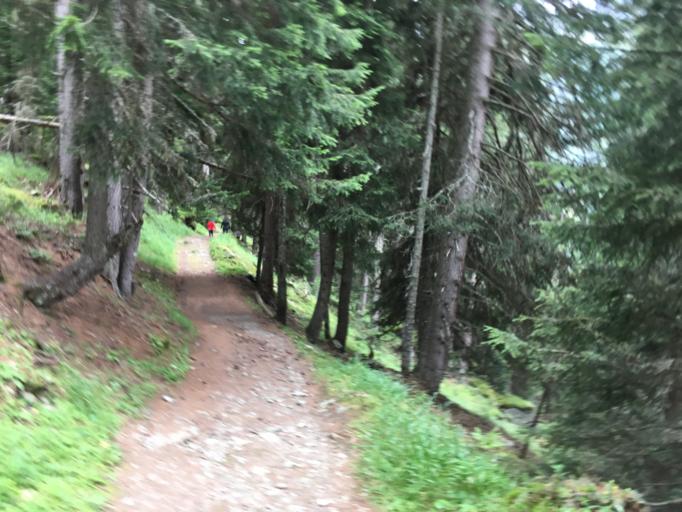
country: CH
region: Grisons
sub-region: Maloja District
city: Silvaplana
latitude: 46.4802
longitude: 9.6486
